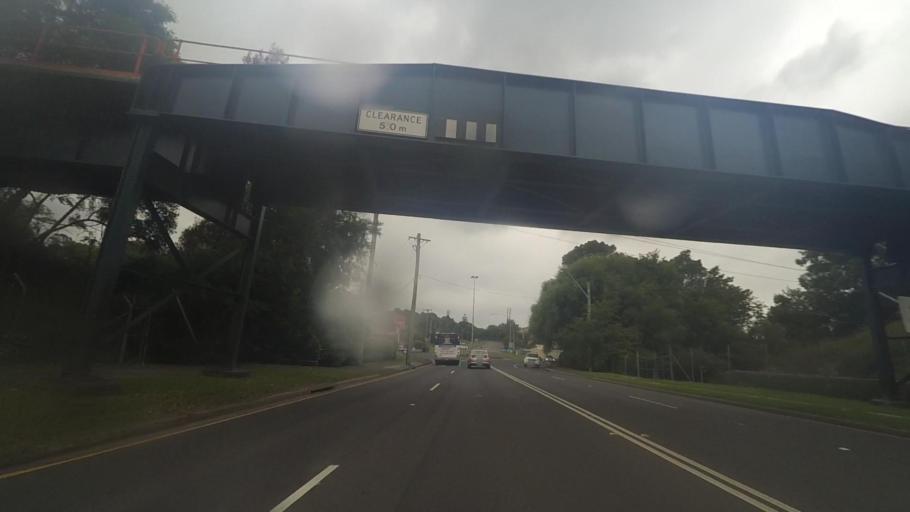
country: AU
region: New South Wales
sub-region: Wollongong
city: Cordeaux Heights
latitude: -34.4478
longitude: 150.8511
